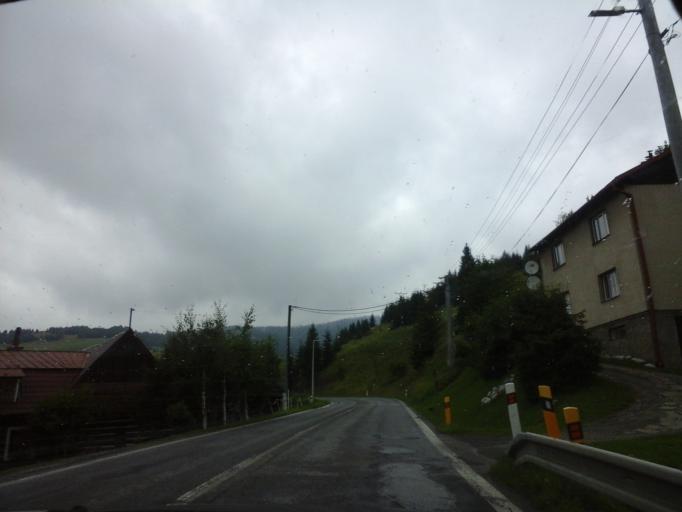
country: SK
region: Presovsky
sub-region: Okres Poprad
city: Zdiar
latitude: 49.2688
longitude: 20.2824
